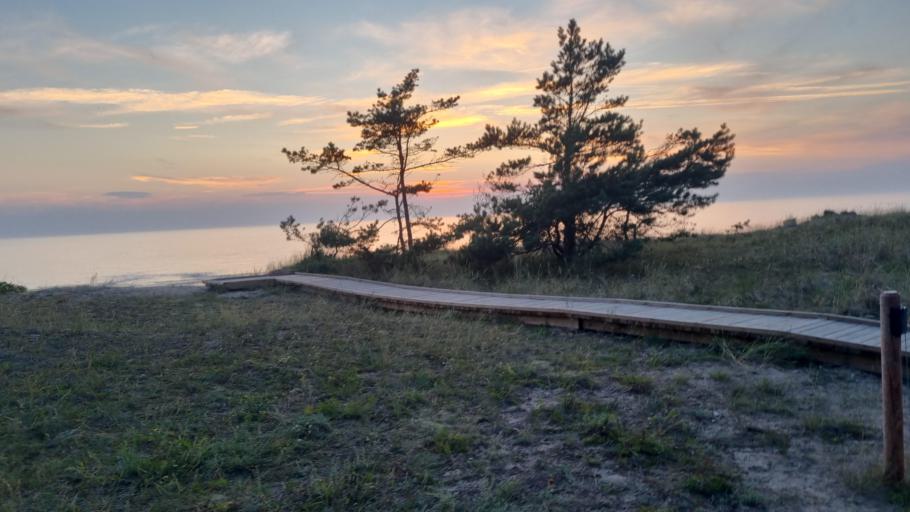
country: LV
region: Ventspils
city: Ventspils
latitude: 57.2472
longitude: 21.4144
